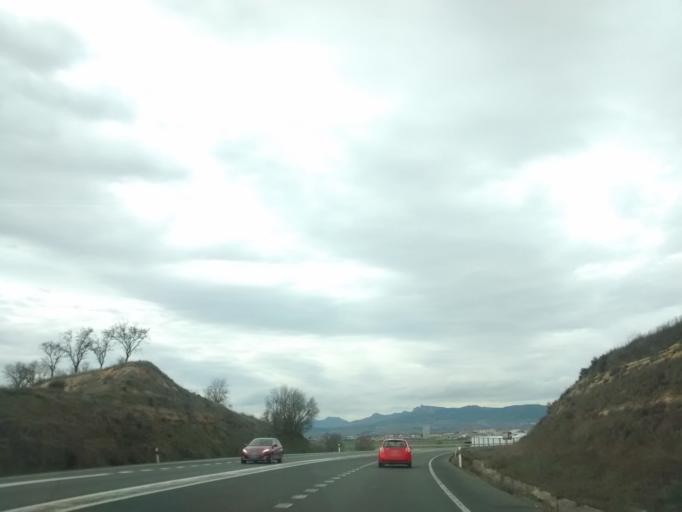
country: ES
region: La Rioja
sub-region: Provincia de La Rioja
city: Ollauri
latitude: 42.5492
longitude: -2.8318
